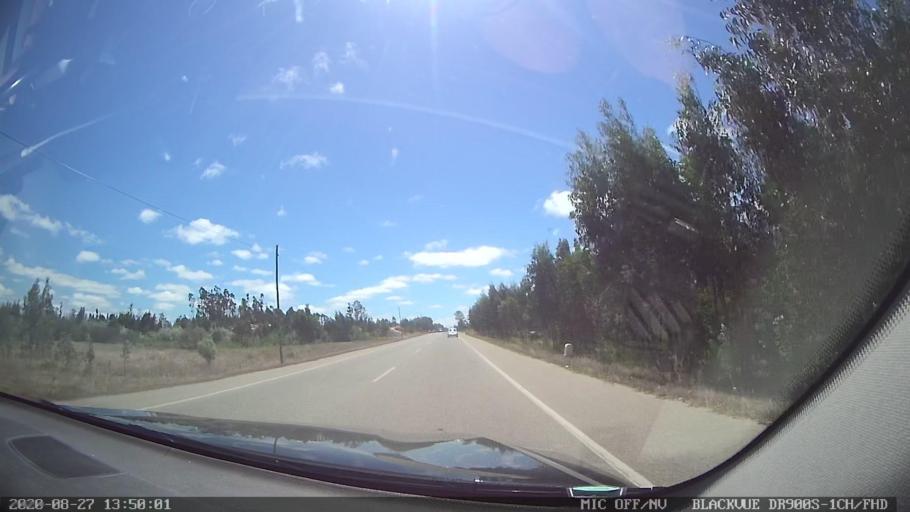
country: PT
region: Coimbra
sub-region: Mira
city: Mira
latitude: 40.3613
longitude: -8.7471
